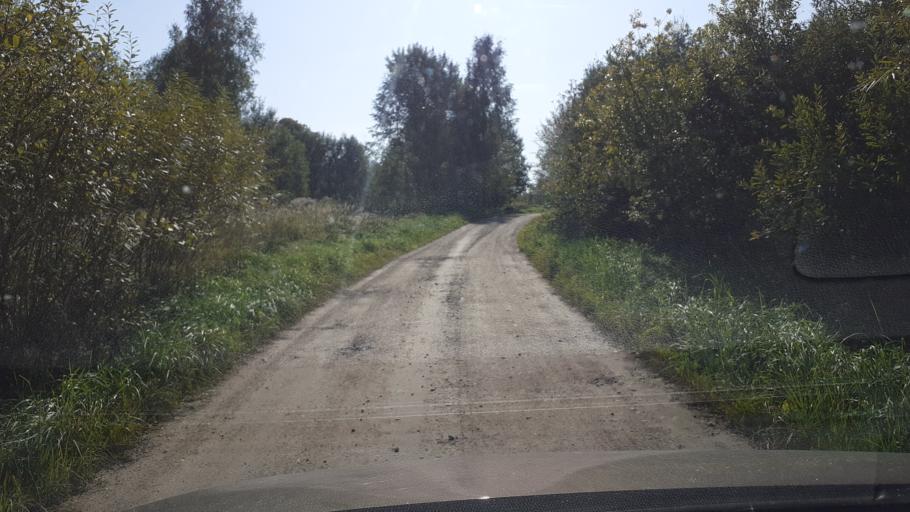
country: LV
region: Kuldigas Rajons
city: Kuldiga
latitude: 56.9491
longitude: 21.9948
